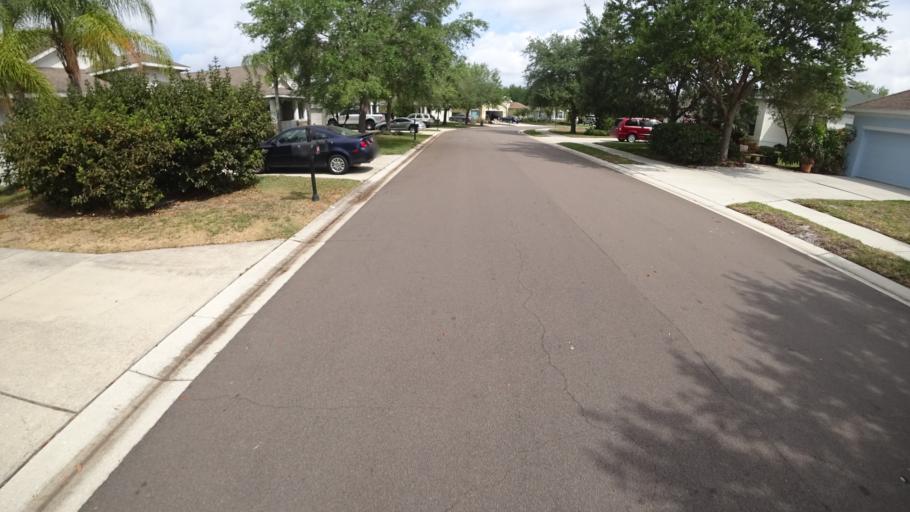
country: US
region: Florida
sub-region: Manatee County
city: Ellenton
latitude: 27.5341
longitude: -82.4198
